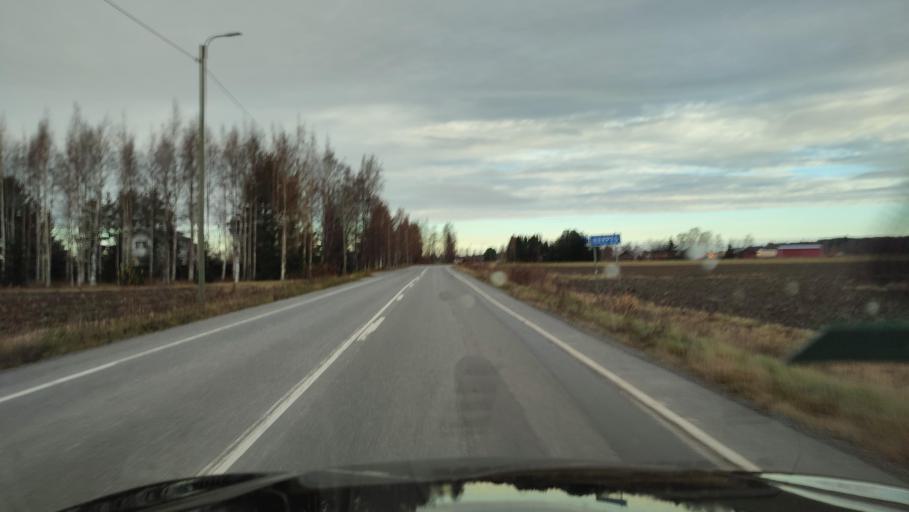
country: FI
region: Ostrobothnia
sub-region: Sydosterbotten
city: Naerpes
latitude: 62.4516
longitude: 21.3531
